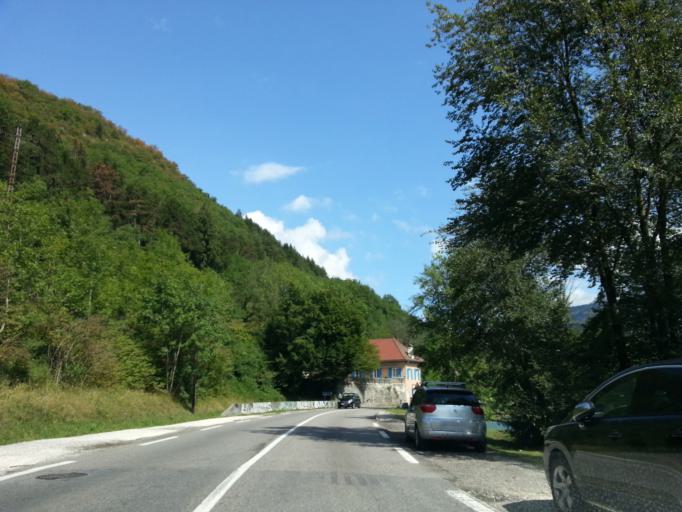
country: FR
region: Rhone-Alpes
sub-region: Departement de la Haute-Savoie
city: Talloires
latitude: 45.8202
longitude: 6.2068
